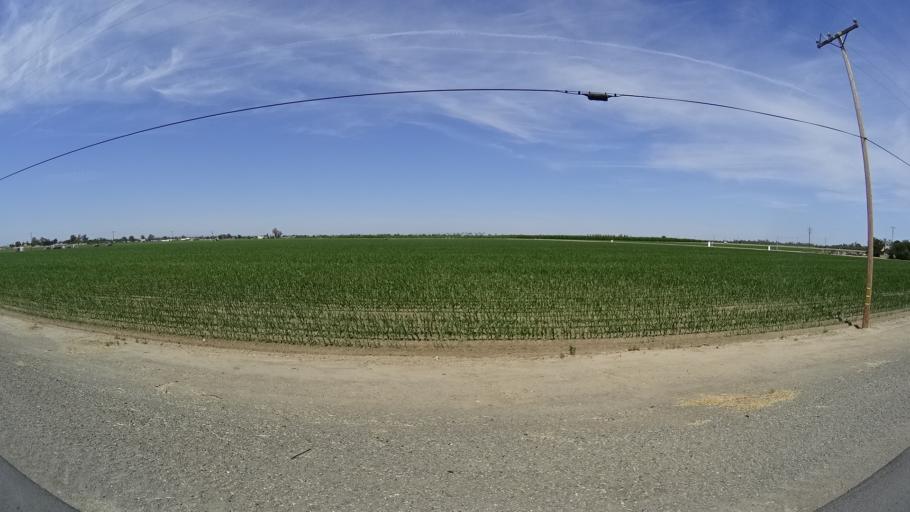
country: US
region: California
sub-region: Kings County
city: Hanford
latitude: 36.3375
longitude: -119.6009
